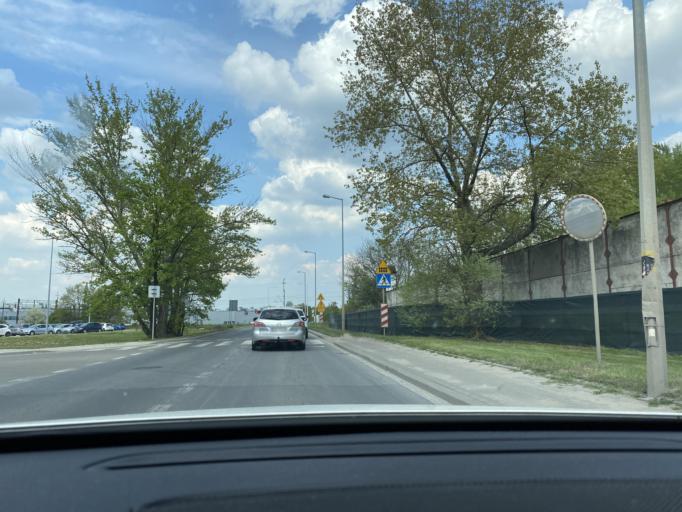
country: PL
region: Lower Silesian Voivodeship
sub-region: Powiat wroclawski
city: Wilczyce
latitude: 51.1195
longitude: 17.1157
